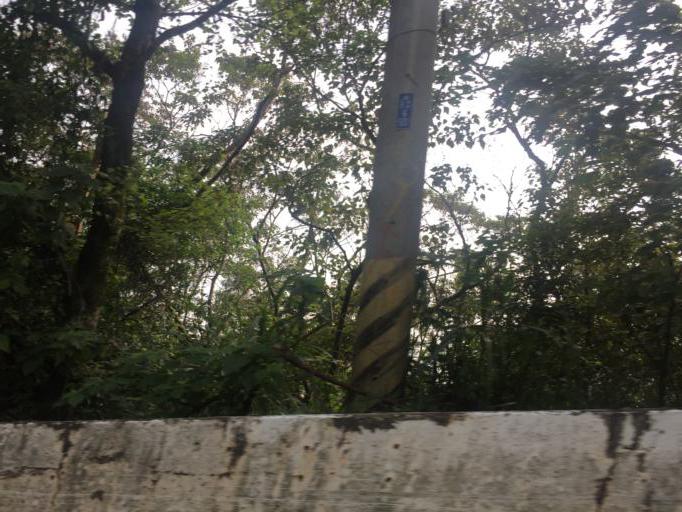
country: TW
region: Taiwan
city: Daxi
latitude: 24.8422
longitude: 121.2114
